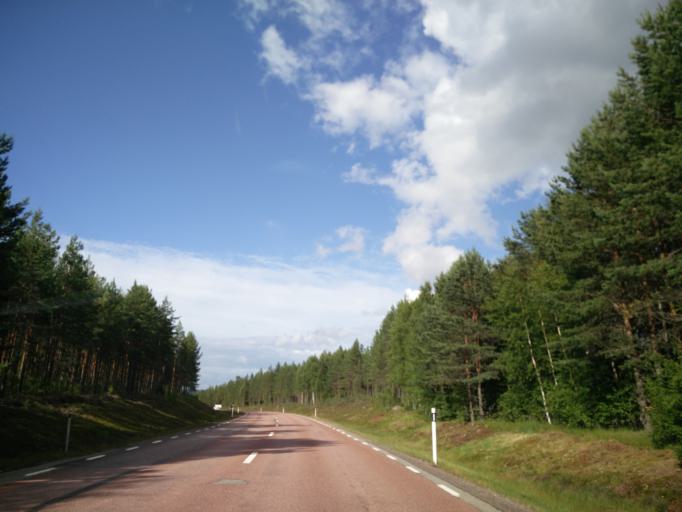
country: SE
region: Vaermland
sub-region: Hagfors Kommun
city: Ekshaerad
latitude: 60.3889
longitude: 13.2592
